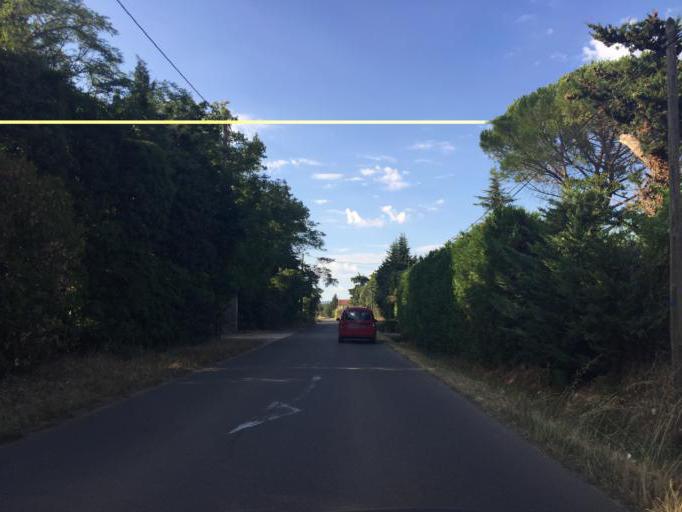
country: FR
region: Provence-Alpes-Cote d'Azur
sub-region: Departement du Vaucluse
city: Pernes-les-Fontaines
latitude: 44.0145
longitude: 5.0551
